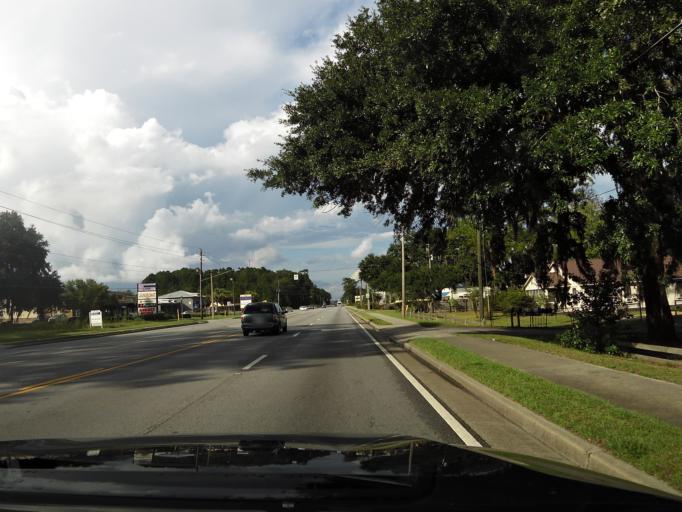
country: US
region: Georgia
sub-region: Liberty County
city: Hinesville
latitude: 31.8094
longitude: -81.6031
